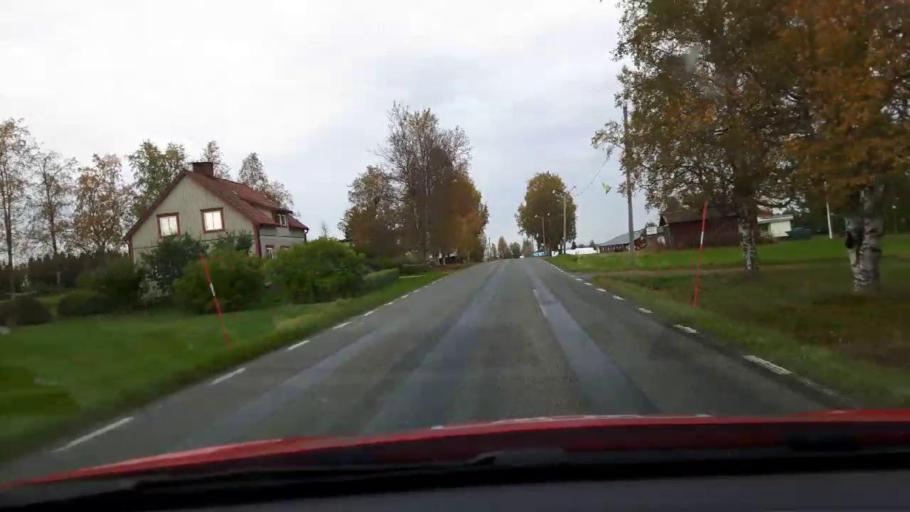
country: SE
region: Jaemtland
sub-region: Bergs Kommun
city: Hoverberg
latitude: 62.8472
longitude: 14.3830
